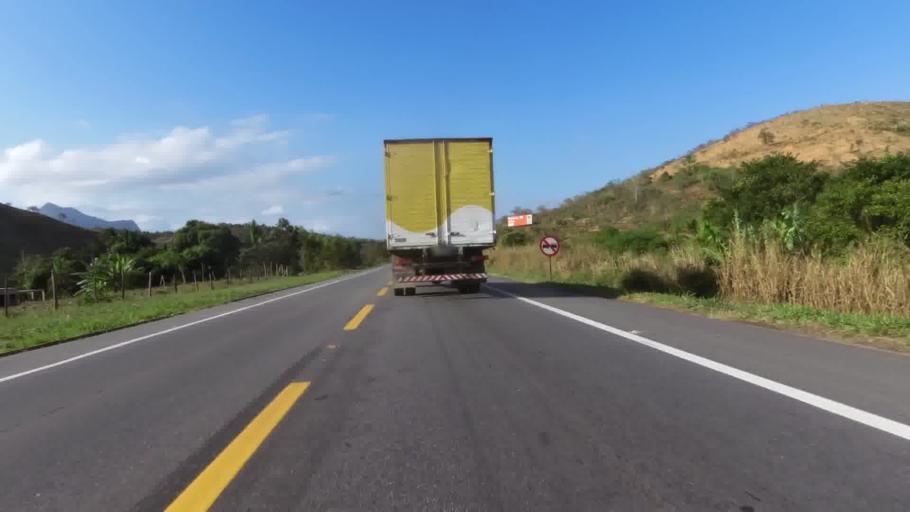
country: BR
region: Espirito Santo
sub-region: Mimoso Do Sul
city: Mimoso do Sul
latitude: -21.1711
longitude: -41.2916
